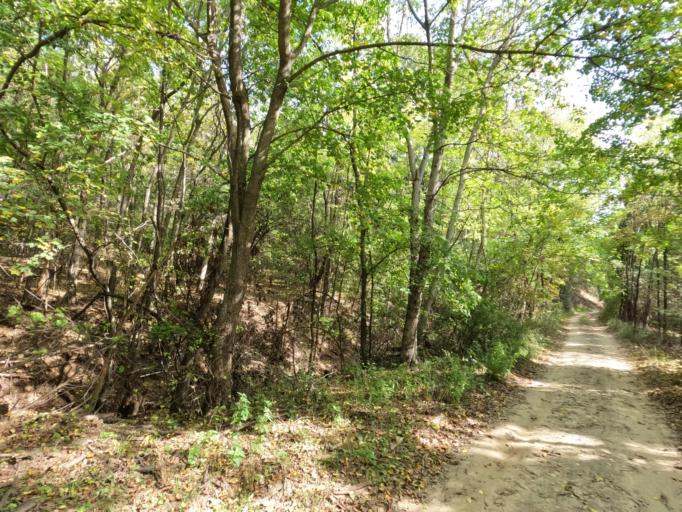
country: HU
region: Tolna
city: Szentgalpuszta
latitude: 46.3462
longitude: 18.6279
